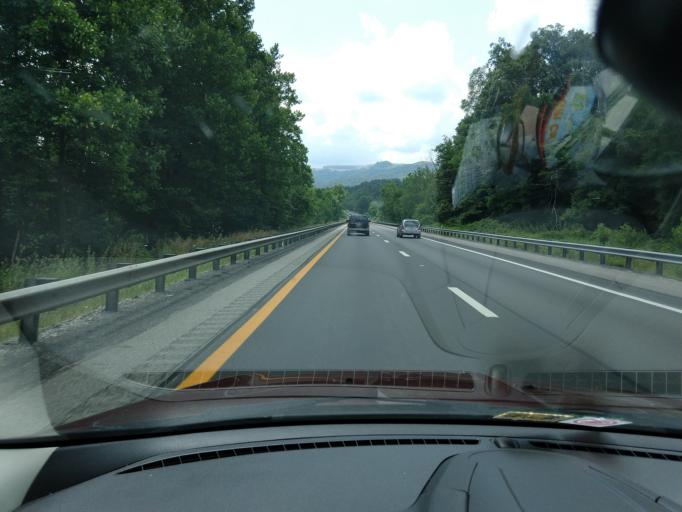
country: US
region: West Virginia
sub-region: Raleigh County
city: Bradley
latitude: 37.9257
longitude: -81.2659
